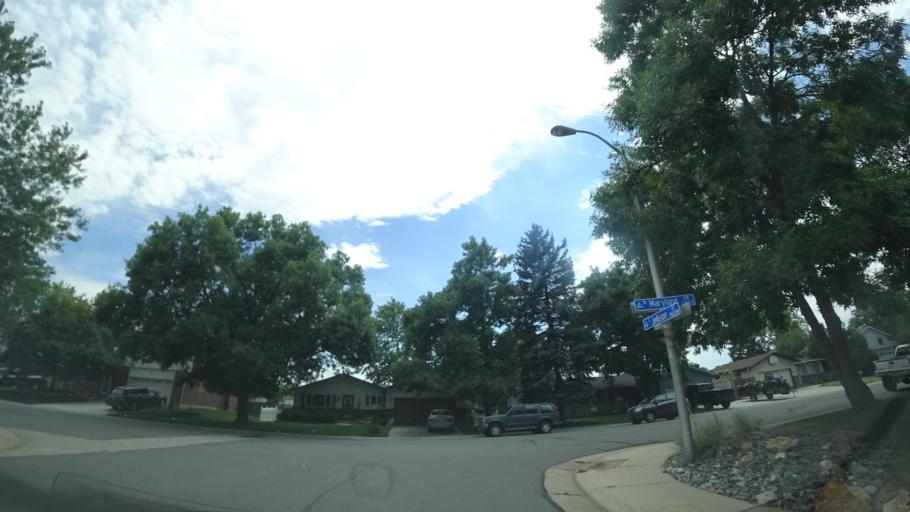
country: US
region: Colorado
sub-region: Jefferson County
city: Lakewood
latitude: 39.6930
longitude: -105.1088
